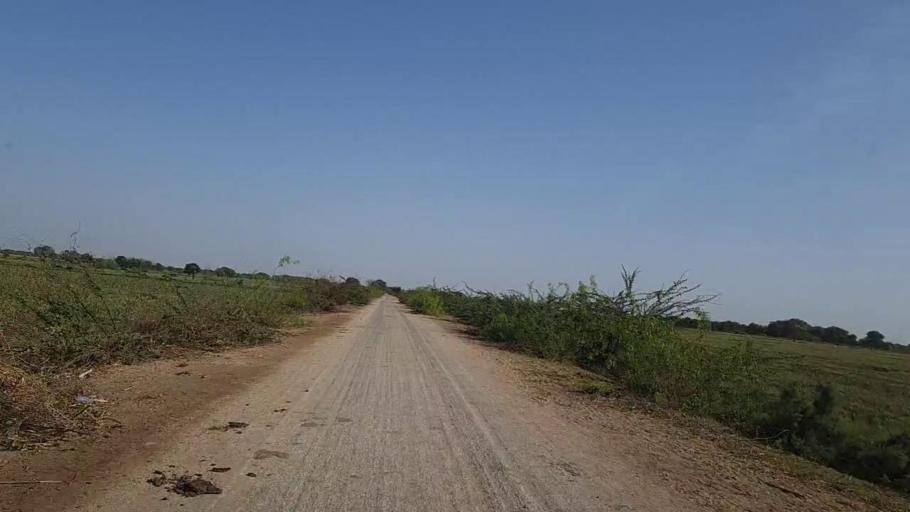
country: PK
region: Sindh
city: Kotri
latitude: 25.1509
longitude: 68.2925
